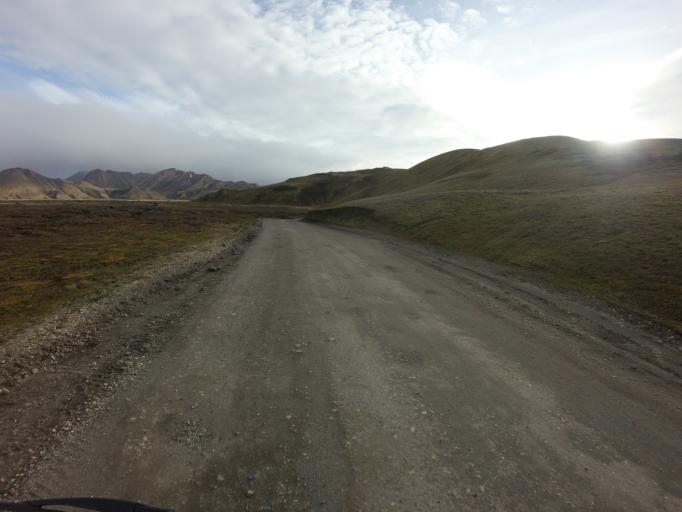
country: IS
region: South
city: Vestmannaeyjar
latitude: 64.0114
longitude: -19.0414
